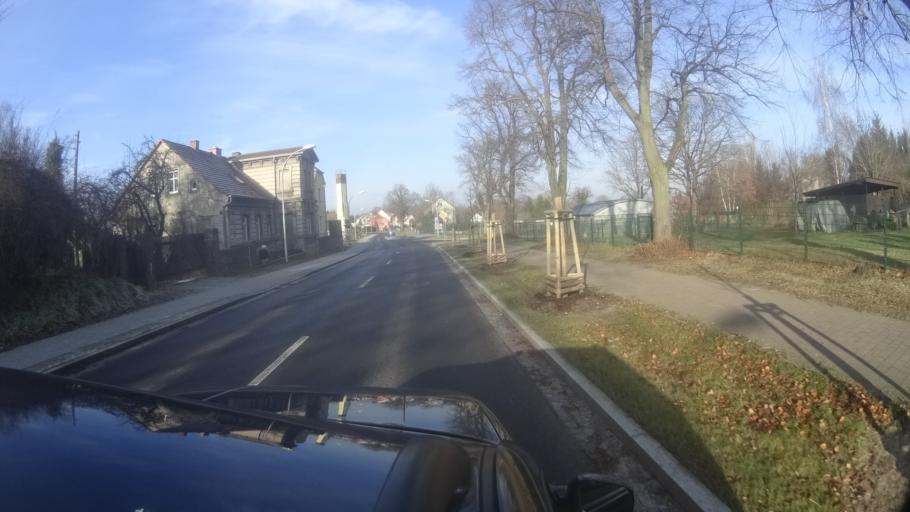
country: DE
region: Brandenburg
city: Kremmen
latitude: 52.7553
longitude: 13.0365
